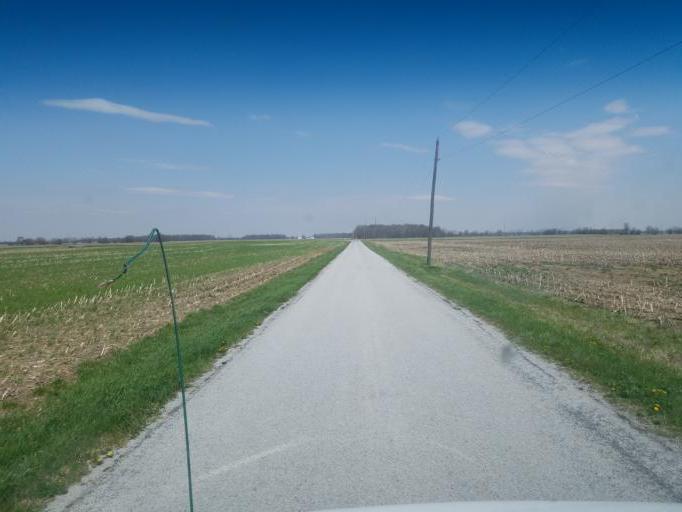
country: US
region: Ohio
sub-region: Hardin County
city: Kenton
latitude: 40.6990
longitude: -83.5473
